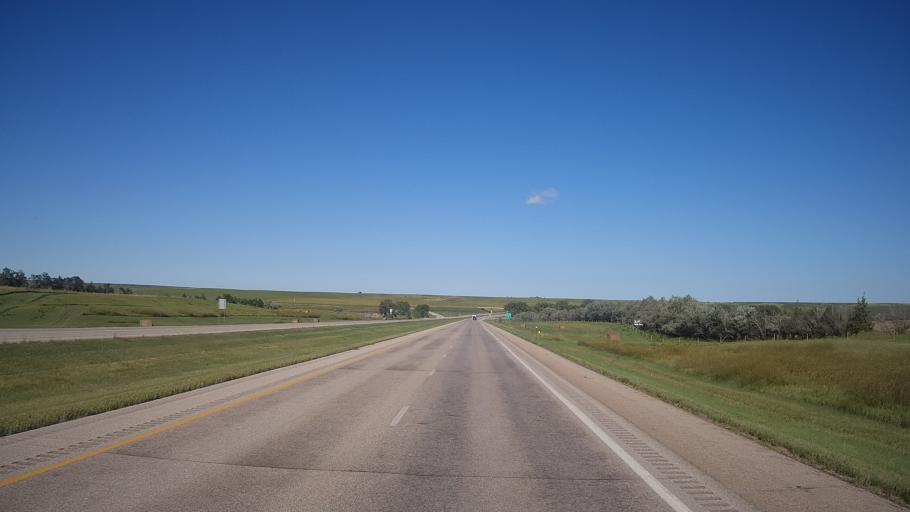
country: US
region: South Dakota
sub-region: Pennington County
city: Box Elder
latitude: 44.1044
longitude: -102.6411
